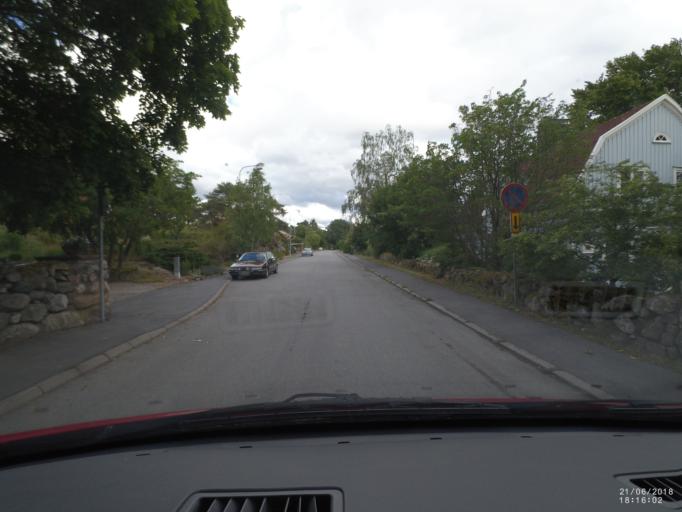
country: SE
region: Soedermanland
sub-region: Nykopings Kommun
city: Nykoping
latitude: 58.7568
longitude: 17.0238
